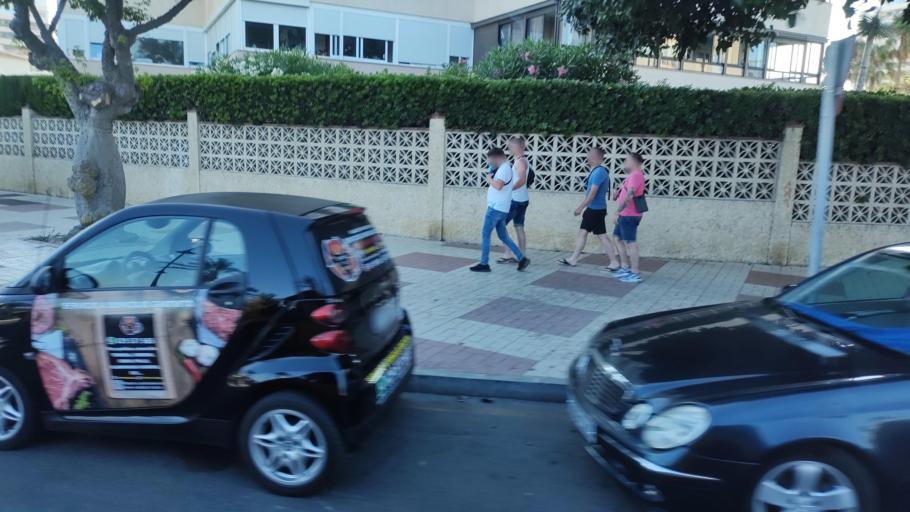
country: ES
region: Andalusia
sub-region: Provincia de Malaga
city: Torremolinos
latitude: 36.6295
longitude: -4.4903
